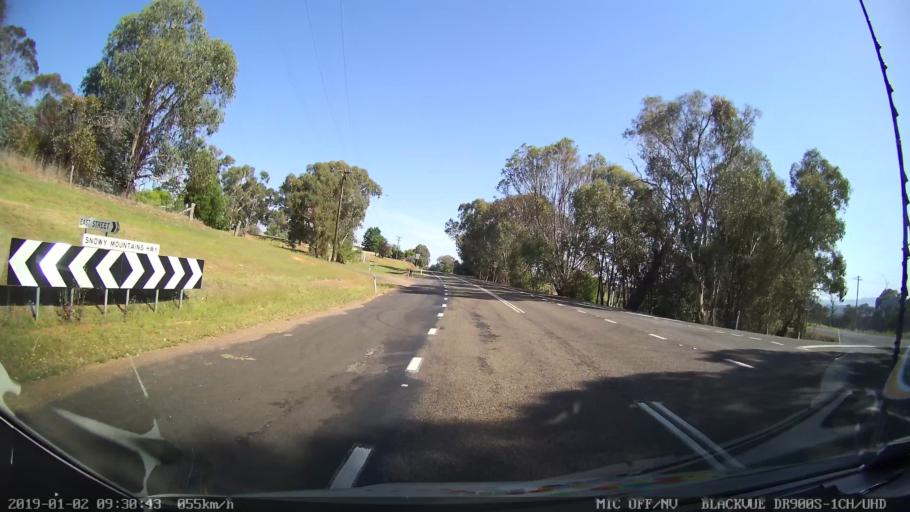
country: AU
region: New South Wales
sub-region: Tumut Shire
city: Tumut
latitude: -35.3243
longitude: 148.2379
